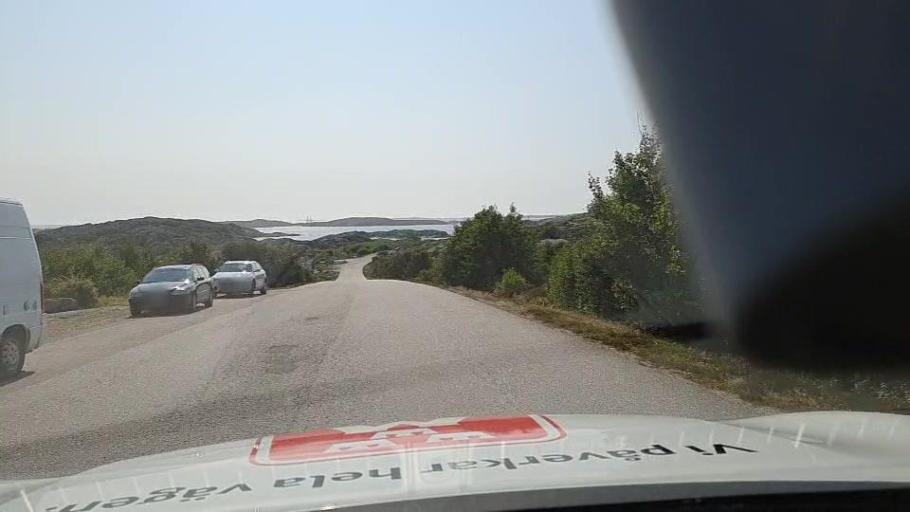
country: SE
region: Vaestra Goetaland
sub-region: Lysekils Kommun
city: Lysekil
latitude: 58.1193
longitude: 11.4601
